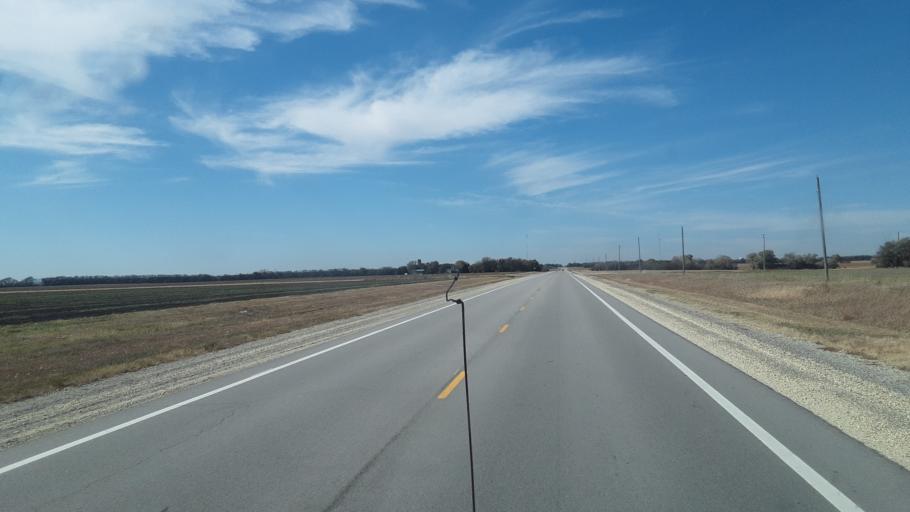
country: US
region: Kansas
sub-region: McPherson County
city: McPherson
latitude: 38.3768
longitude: -97.5710
